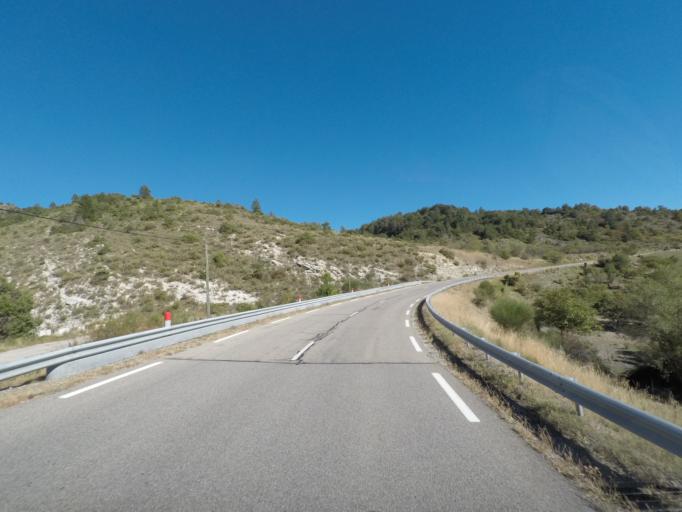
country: FR
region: Provence-Alpes-Cote d'Azur
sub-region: Departement des Hautes-Alpes
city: Serres
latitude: 44.4064
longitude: 5.5207
